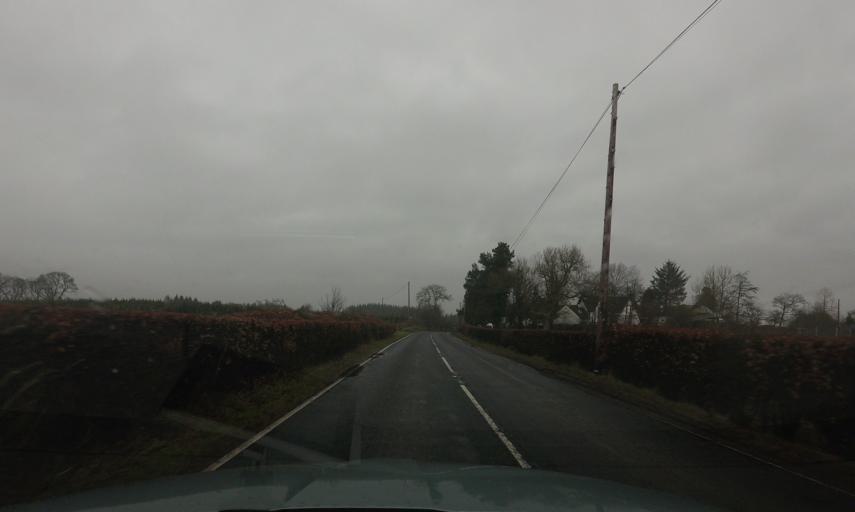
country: GB
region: Scotland
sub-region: Stirling
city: Balfron
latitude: 56.1100
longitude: -4.3585
